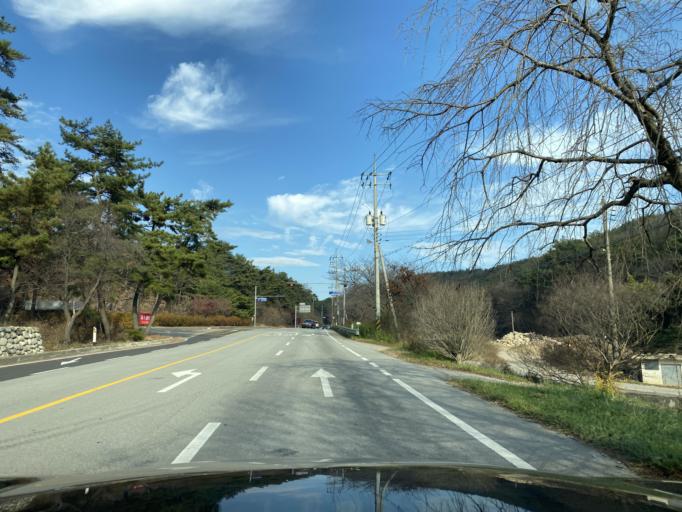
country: KR
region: Chungcheongnam-do
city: Hongsung
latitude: 36.6563
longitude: 126.6241
